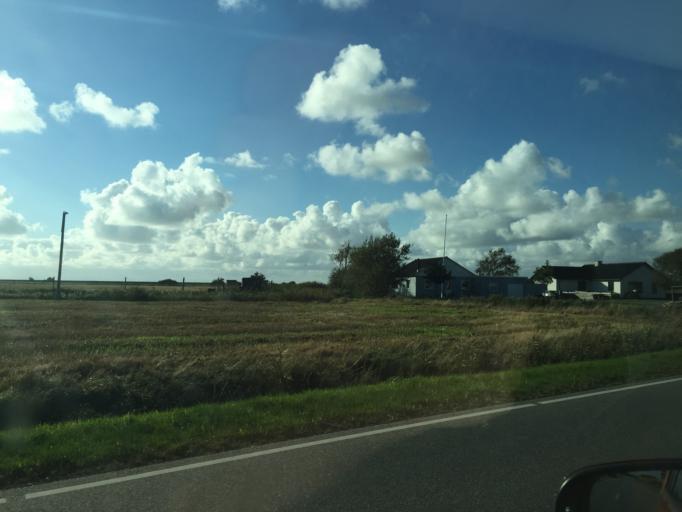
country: DE
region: Schleswig-Holstein
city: Rodenas
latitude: 54.9728
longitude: 8.6998
